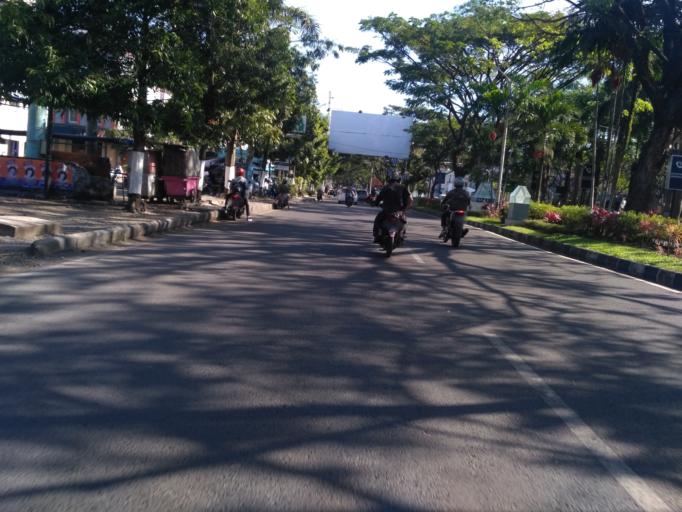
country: ID
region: East Java
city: Malang
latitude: -7.9424
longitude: 112.6217
